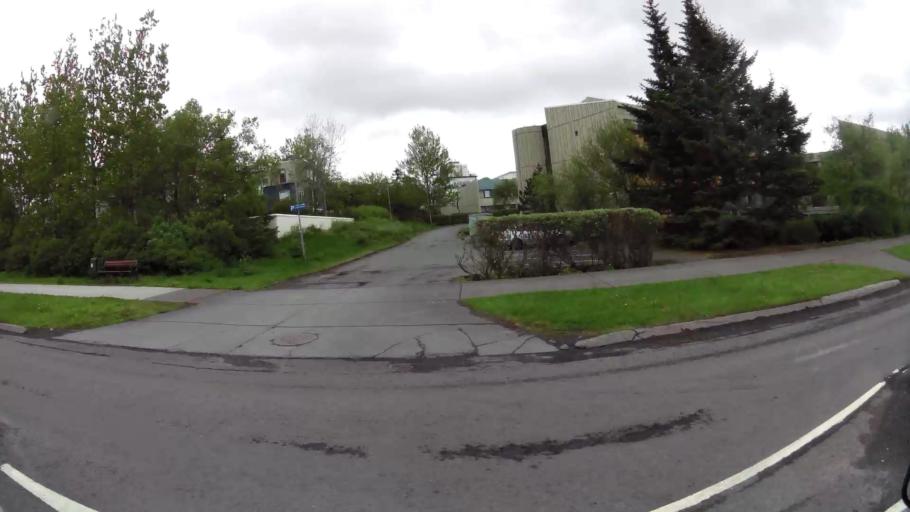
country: IS
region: Capital Region
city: Reykjavik
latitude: 64.1478
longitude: -21.8746
